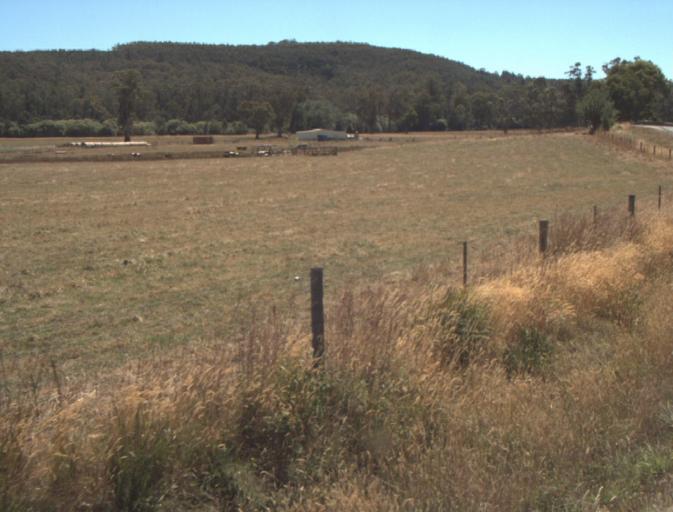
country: AU
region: Tasmania
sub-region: Launceston
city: Newstead
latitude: -41.3301
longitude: 147.3531
